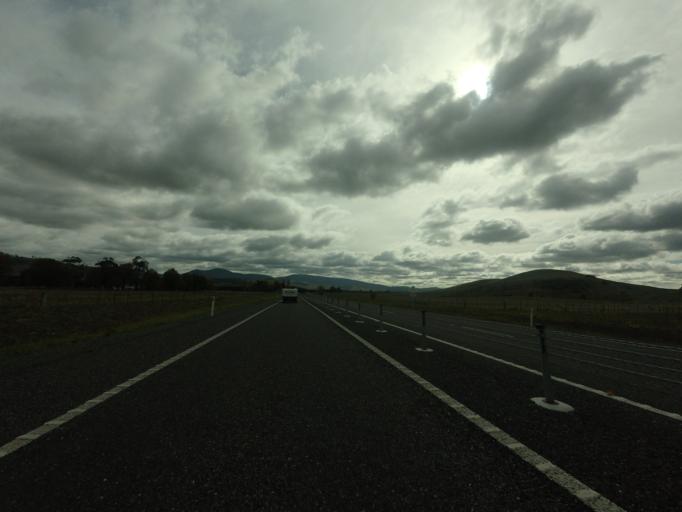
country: AU
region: Tasmania
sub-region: Brighton
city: Bridgewater
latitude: -42.5234
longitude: 147.1969
